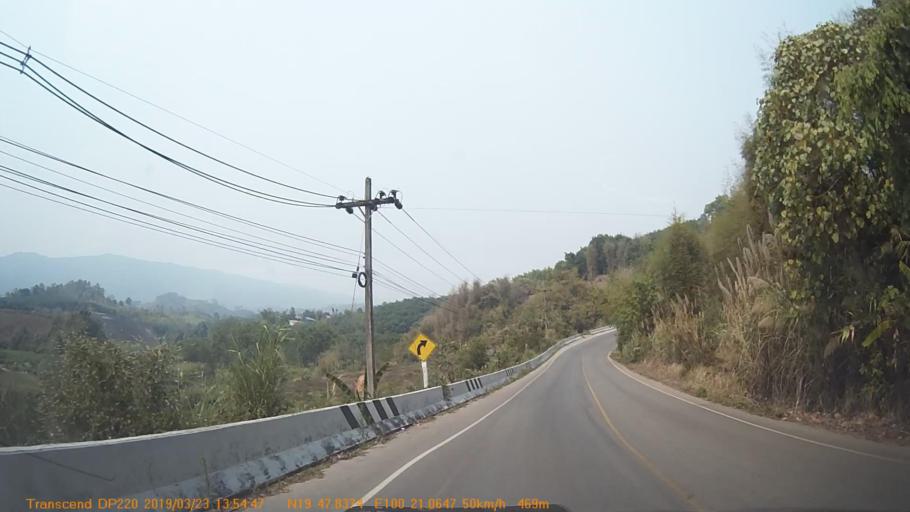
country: TH
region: Chiang Rai
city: Khun Tan
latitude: 19.7976
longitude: 100.3511
